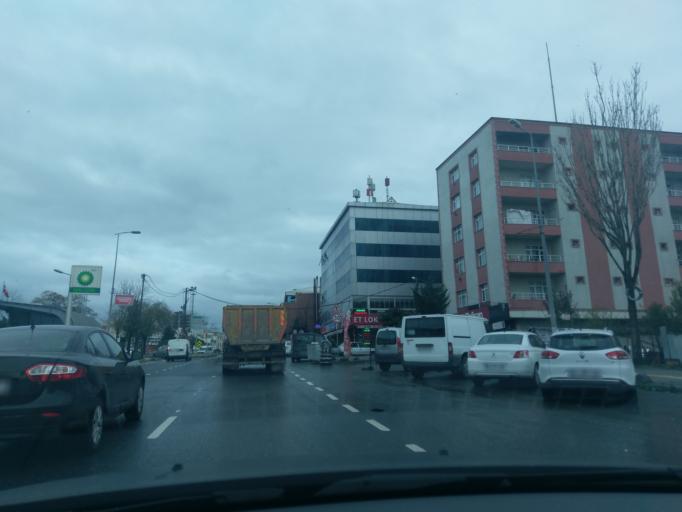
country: TR
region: Istanbul
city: Mahmutbey
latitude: 41.0567
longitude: 28.8306
